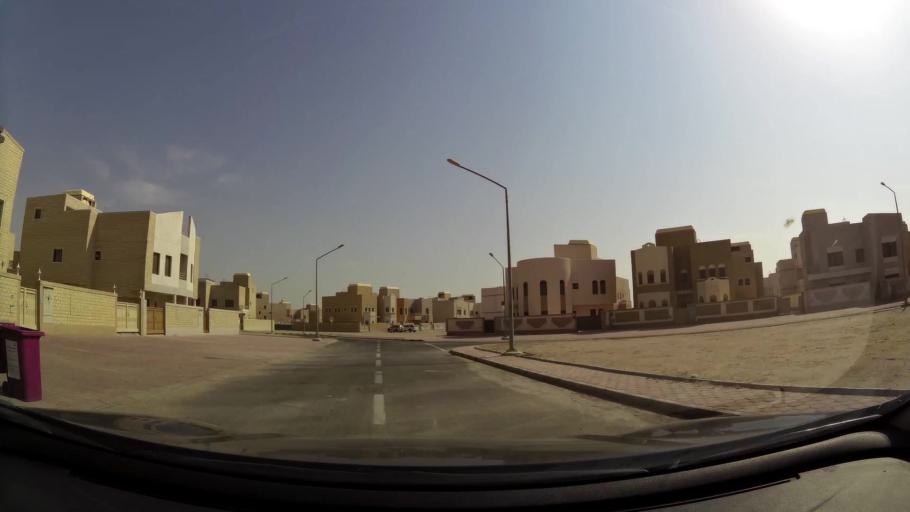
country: KW
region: Al Ahmadi
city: Al Wafrah
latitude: 28.7960
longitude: 48.0707
